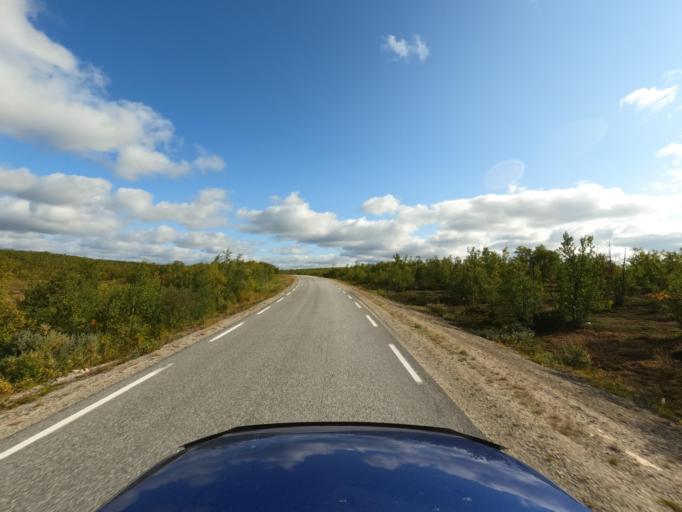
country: NO
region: Finnmark Fylke
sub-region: Porsanger
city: Lakselv
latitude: 69.3915
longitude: 24.5413
